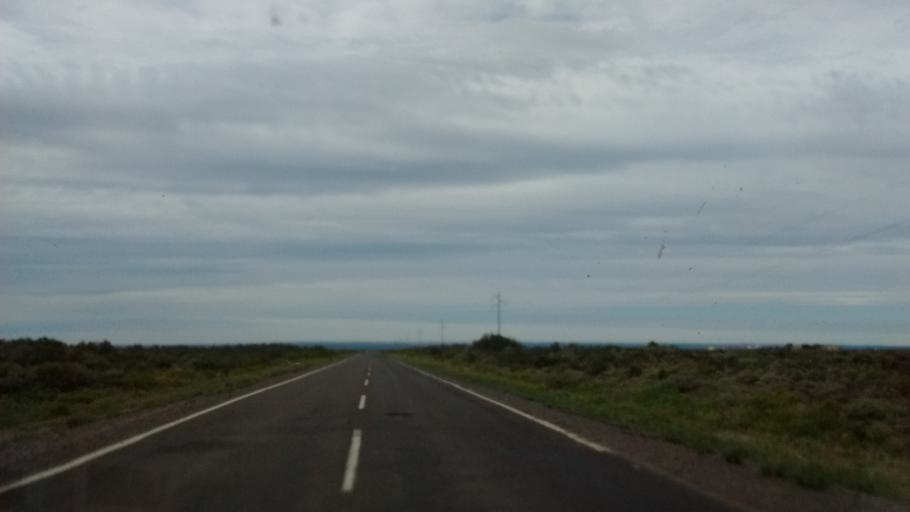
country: AR
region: Rio Negro
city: Catriel
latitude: -37.9607
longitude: -67.8965
